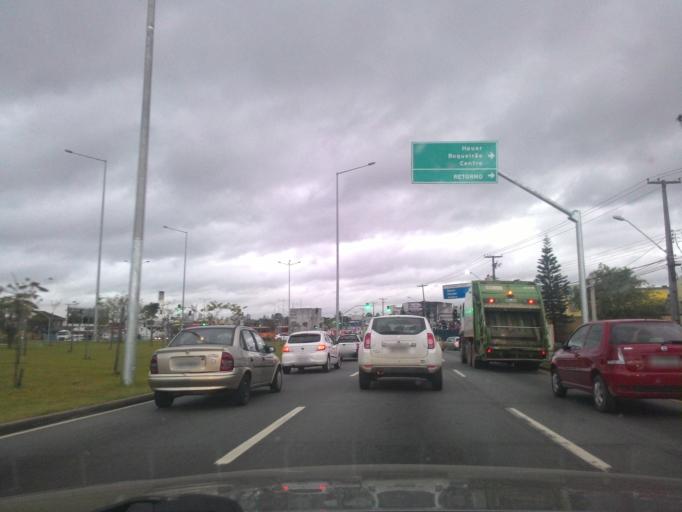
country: BR
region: Parana
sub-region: Curitiba
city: Curitiba
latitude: -25.4763
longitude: -49.2594
